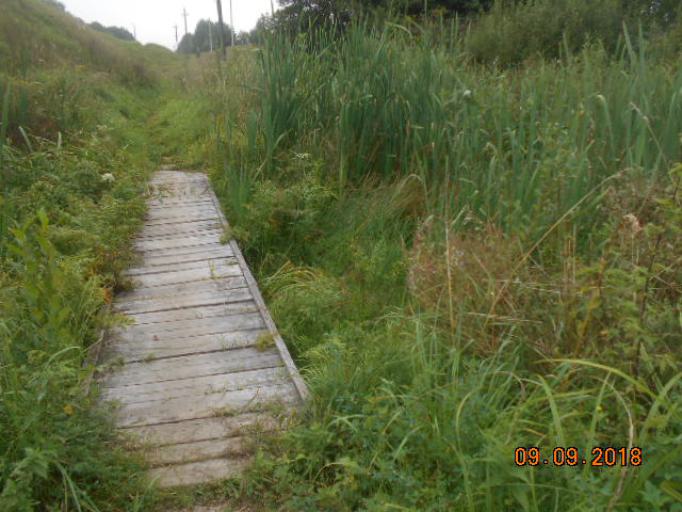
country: BY
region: Brest
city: Baranovichi
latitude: 53.1204
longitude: 25.6922
